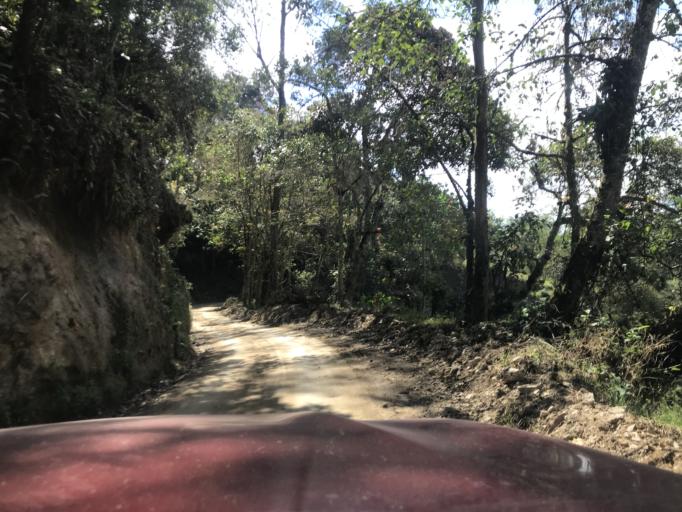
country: PE
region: Cajamarca
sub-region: Provincia de Chota
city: Querocoto
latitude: -6.3456
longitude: -79.0462
